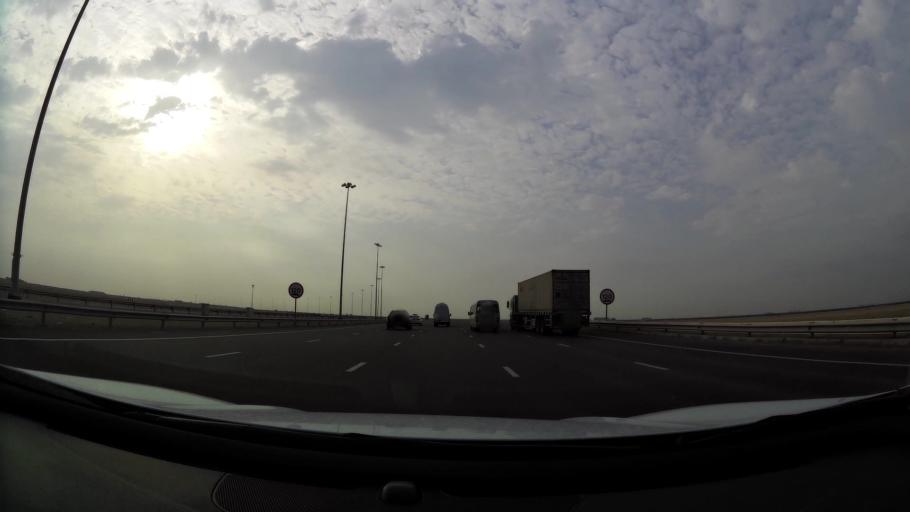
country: AE
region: Abu Dhabi
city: Abu Dhabi
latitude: 24.5357
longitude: 54.4858
